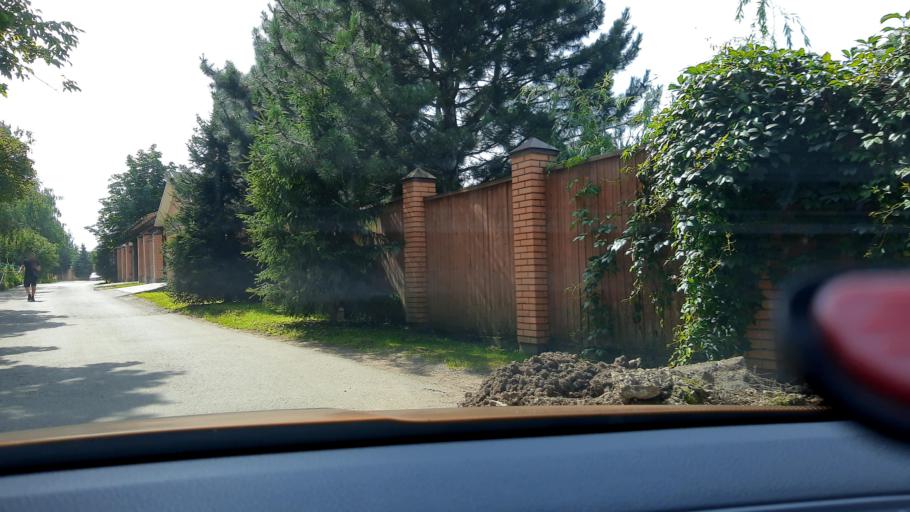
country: RU
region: Moskovskaya
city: Nemchinovka
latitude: 55.7149
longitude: 37.3637
